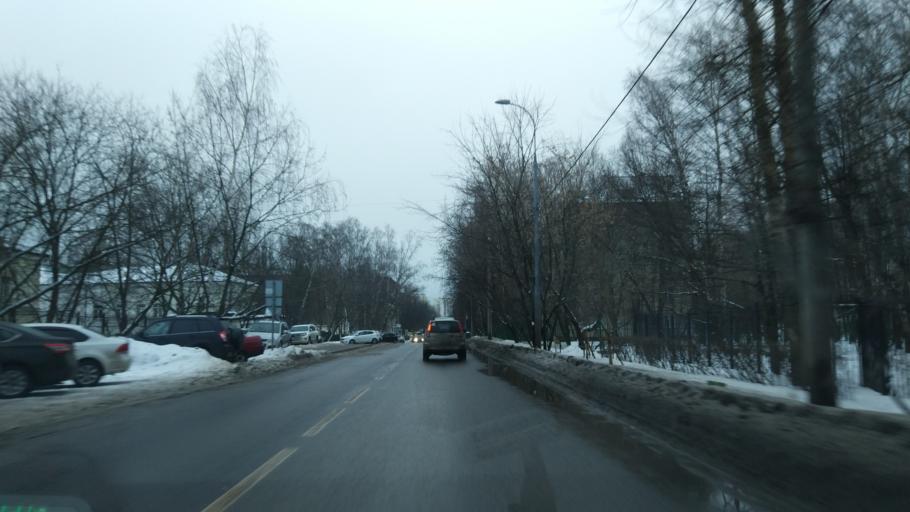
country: RU
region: Moskovskaya
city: Izmaylovo
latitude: 55.7896
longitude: 37.8235
